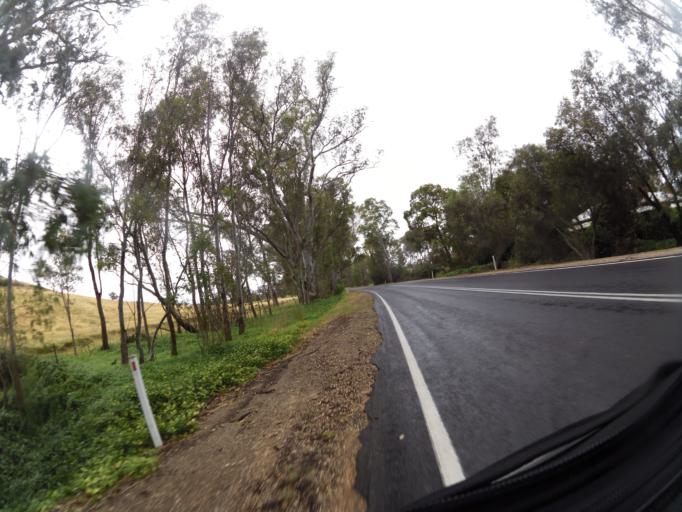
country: AU
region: Victoria
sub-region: Mount Alexander
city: Castlemaine
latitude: -37.1667
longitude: 144.0404
